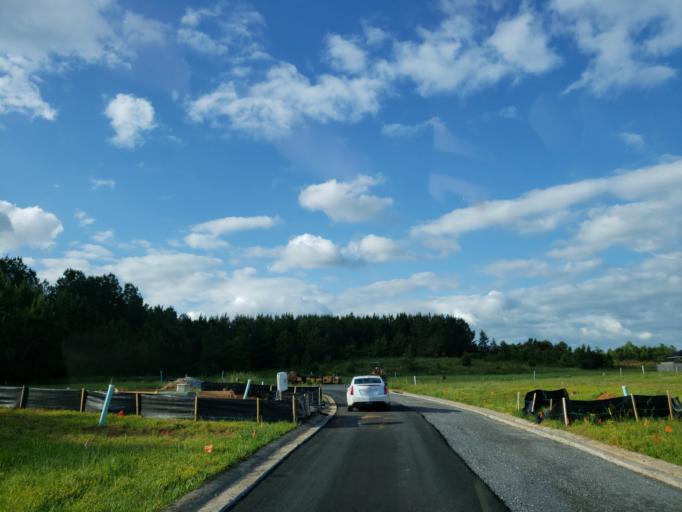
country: US
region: Georgia
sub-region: Bartow County
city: Adairsville
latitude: 34.3886
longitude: -84.8992
